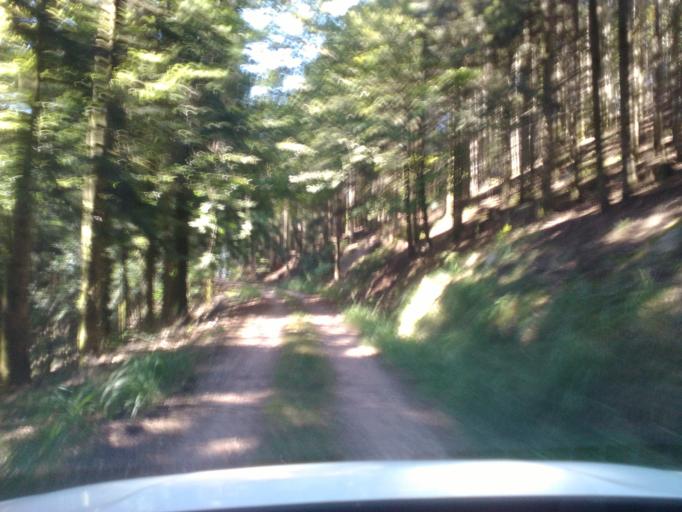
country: FR
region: Lorraine
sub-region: Departement des Vosges
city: Senones
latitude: 48.4361
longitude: 6.9774
